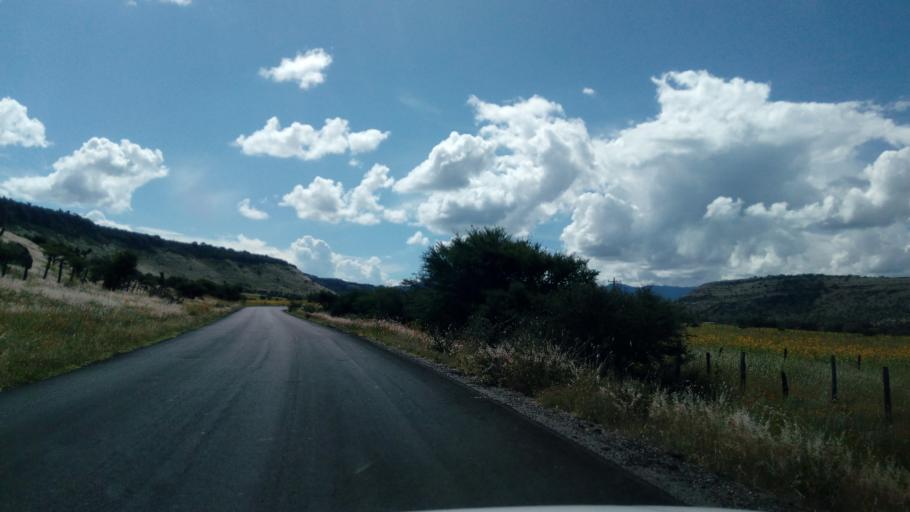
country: MX
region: Durango
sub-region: Durango
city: Jose Refugio Salcido
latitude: 23.8280
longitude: -104.4824
